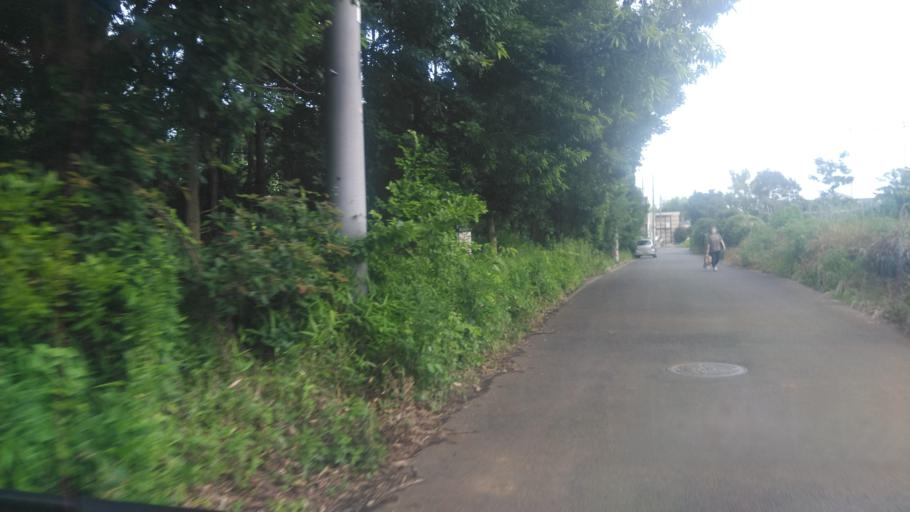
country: JP
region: Kanagawa
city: Fujisawa
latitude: 35.3963
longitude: 139.4375
